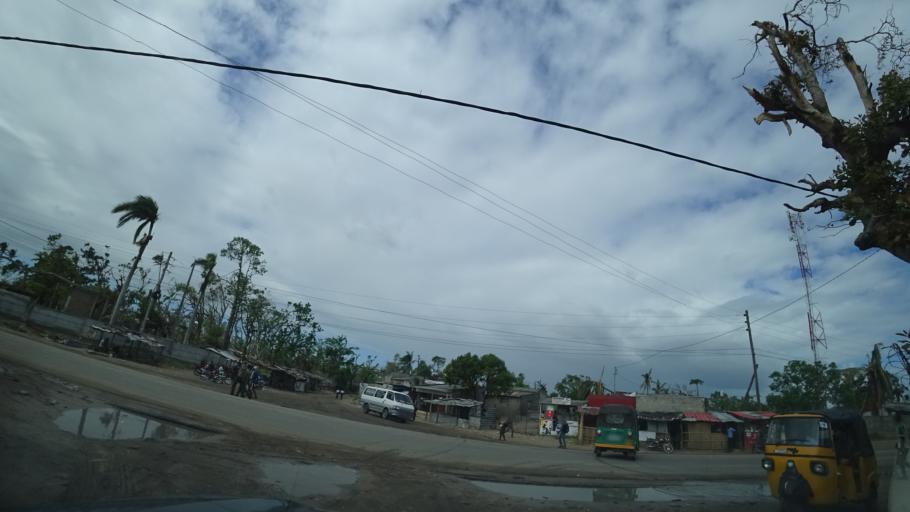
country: MZ
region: Sofala
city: Beira
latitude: -19.8067
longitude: 34.9052
